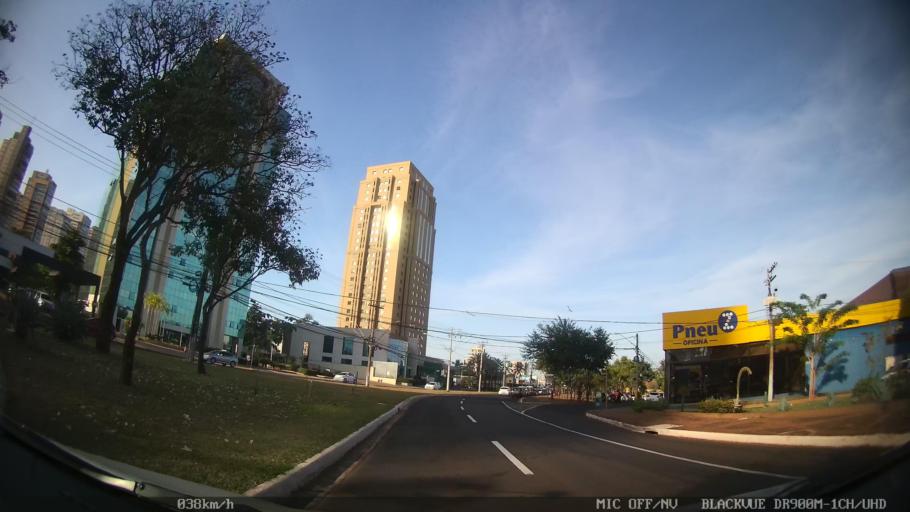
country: BR
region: Sao Paulo
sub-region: Ribeirao Preto
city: Ribeirao Preto
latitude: -21.2047
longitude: -47.8107
